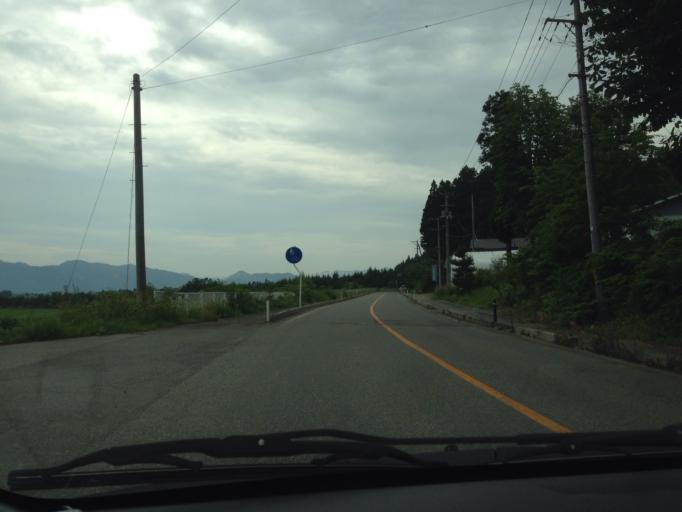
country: JP
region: Fukushima
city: Inawashiro
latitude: 37.5482
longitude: 140.0595
